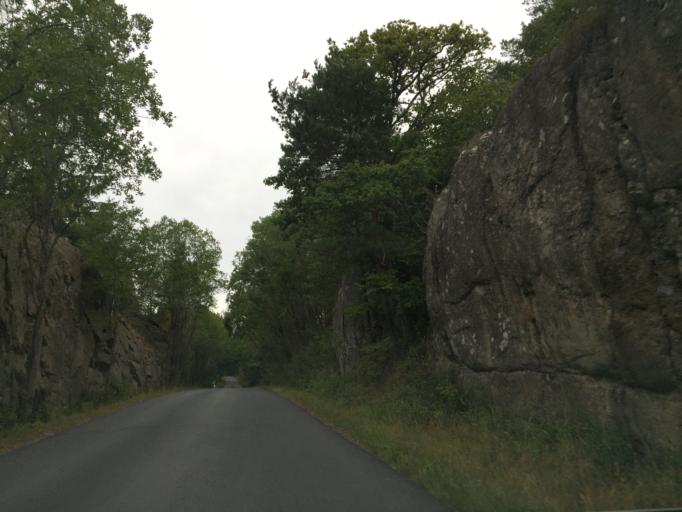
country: NO
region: Ostfold
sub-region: Hvaler
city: Skjaerhalden
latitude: 59.0674
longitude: 11.0317
